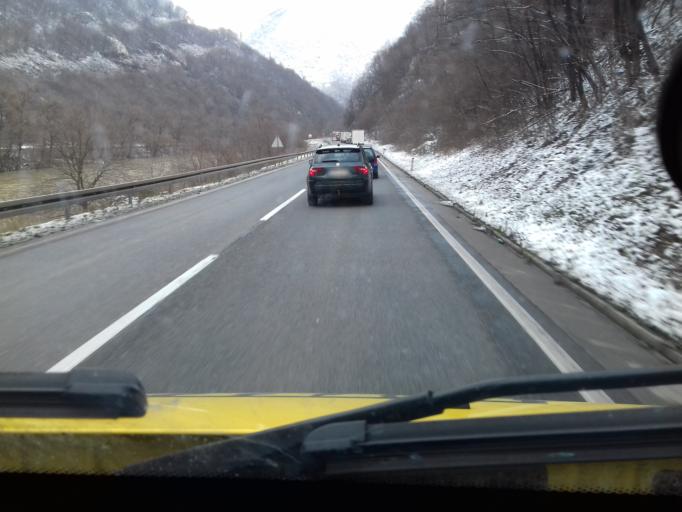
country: BA
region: Federation of Bosnia and Herzegovina
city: Lokvine
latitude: 44.2819
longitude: 17.8846
